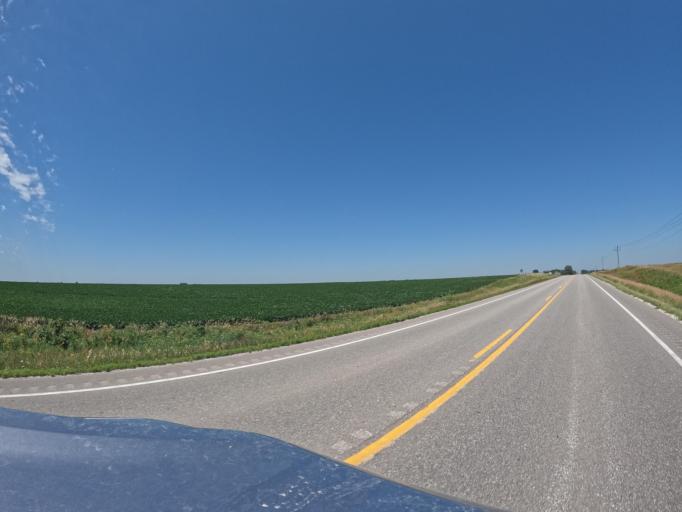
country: US
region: Iowa
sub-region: Keokuk County
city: Sigourney
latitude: 41.4536
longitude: -92.3551
